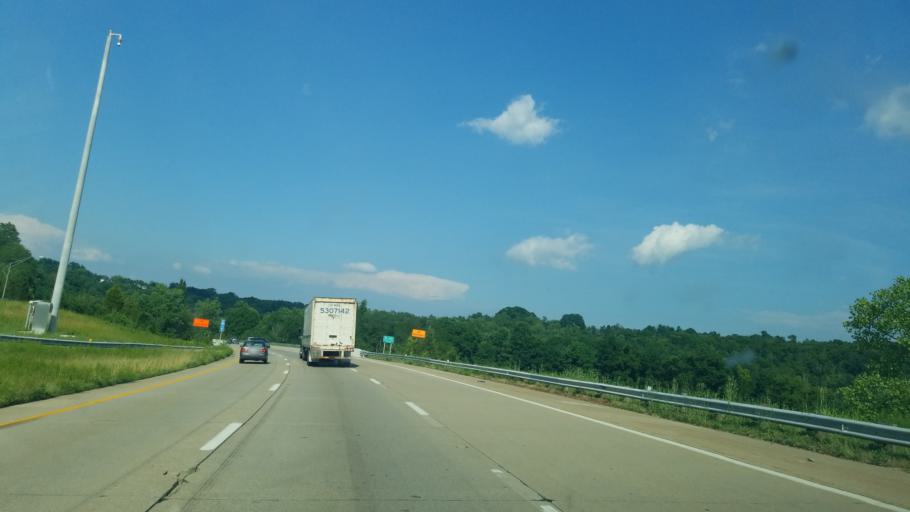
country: US
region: Kentucky
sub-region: Campbell County
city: Silver Grove
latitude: 39.0546
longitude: -84.3929
